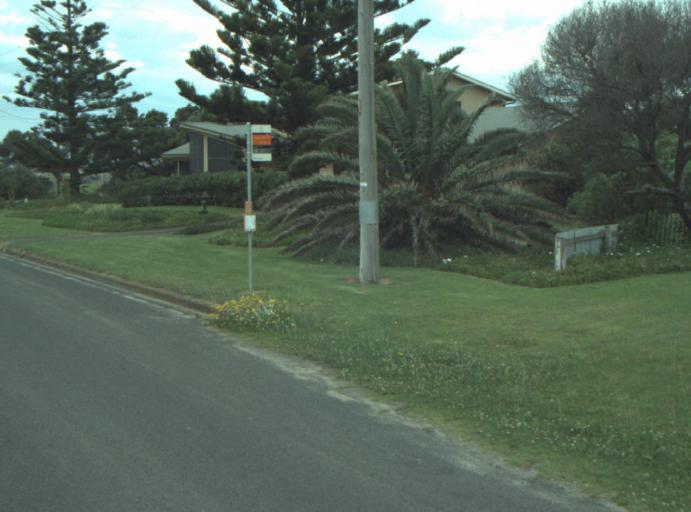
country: AU
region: Victoria
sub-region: Greater Geelong
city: Clifton Springs
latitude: -38.1203
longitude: 144.6918
